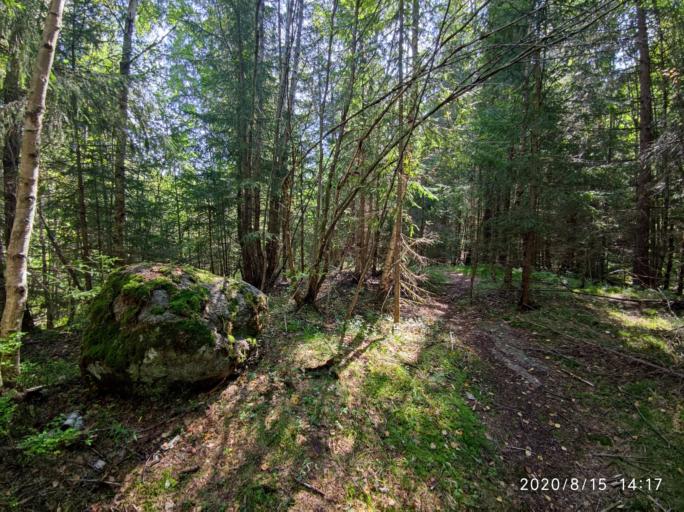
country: NO
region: Akershus
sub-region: Nittedal
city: Rotnes
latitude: 60.0621
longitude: 10.8490
